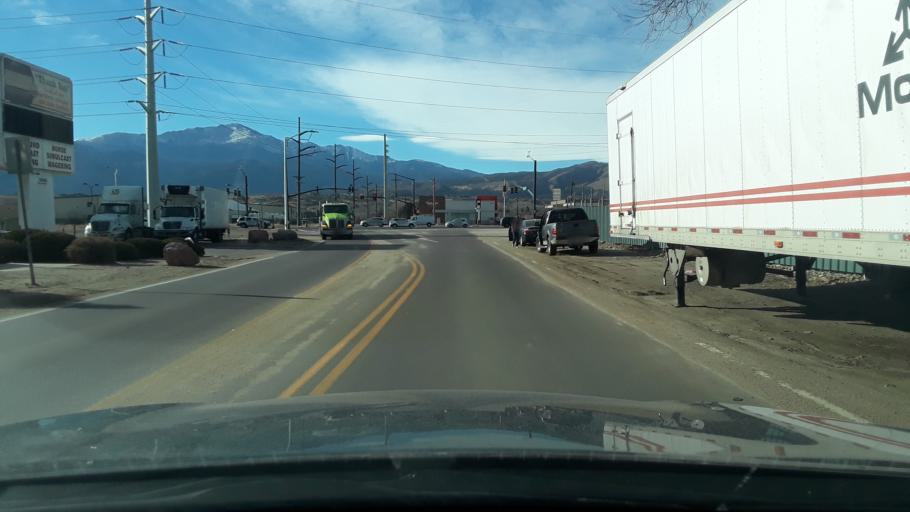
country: US
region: Colorado
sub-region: El Paso County
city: Colorado Springs
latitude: 38.8861
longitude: -104.8174
